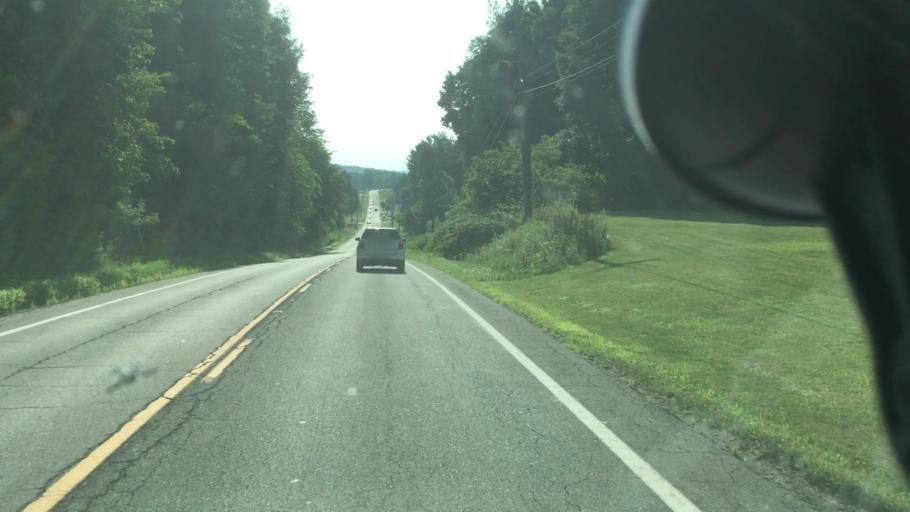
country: US
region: Ohio
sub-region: Mahoning County
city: Lowellville
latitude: 41.0239
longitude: -80.5322
